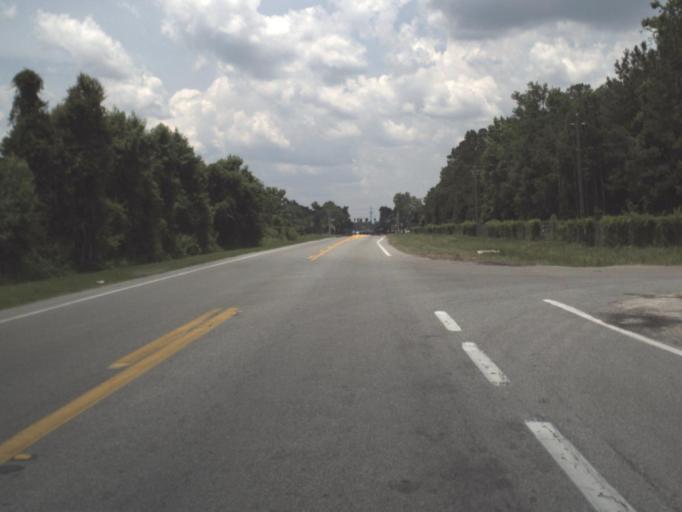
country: US
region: Florida
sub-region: Columbia County
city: Watertown
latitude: 30.1769
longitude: -82.5901
